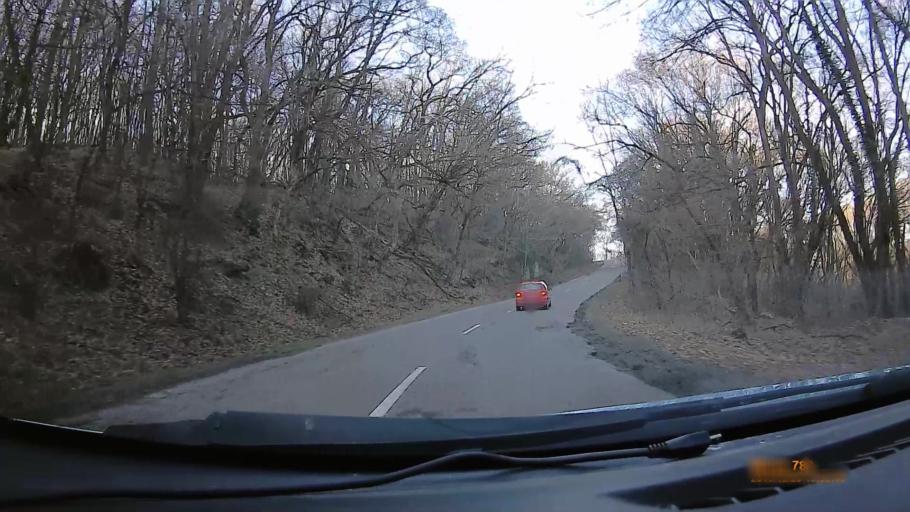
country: HU
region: Heves
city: Sirok
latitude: 47.8929
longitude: 20.1884
